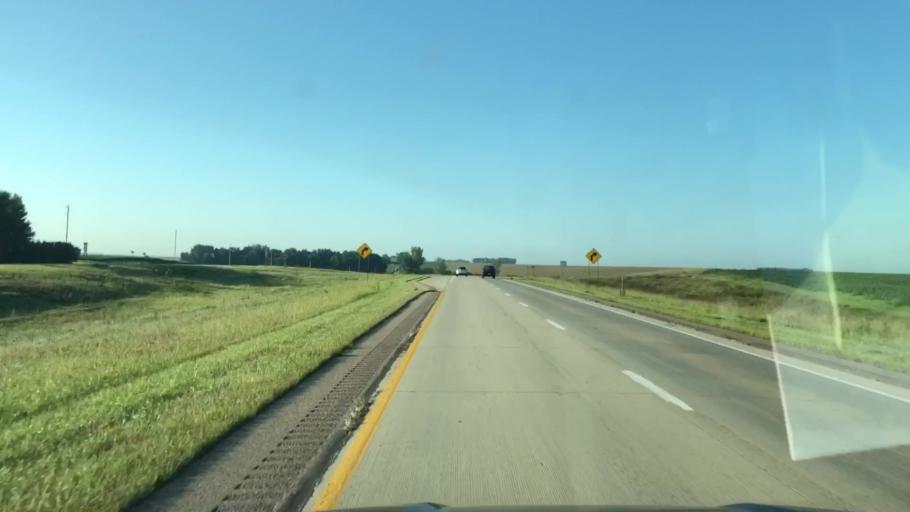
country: US
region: Iowa
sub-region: Sioux County
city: Alton
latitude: 43.0415
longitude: -95.9200
